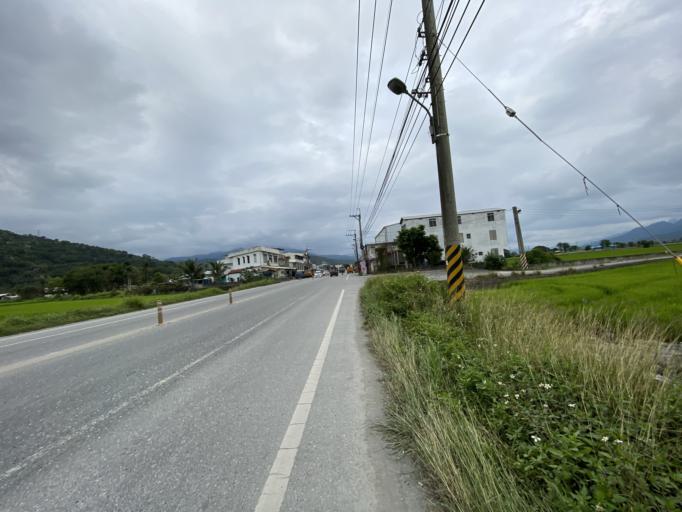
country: TW
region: Taiwan
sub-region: Taitung
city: Taitung
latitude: 23.3816
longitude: 121.3298
